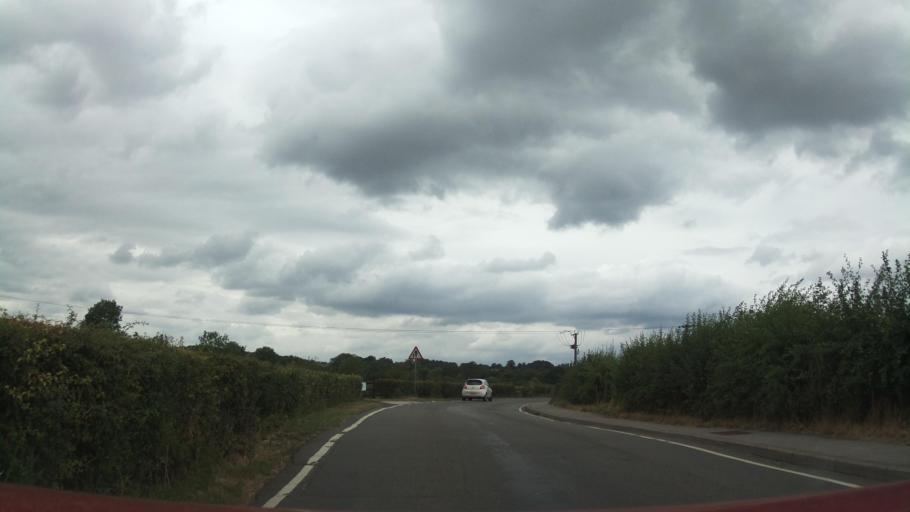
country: GB
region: England
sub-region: Derbyshire
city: Long Eaton
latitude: 52.9064
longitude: -1.3191
